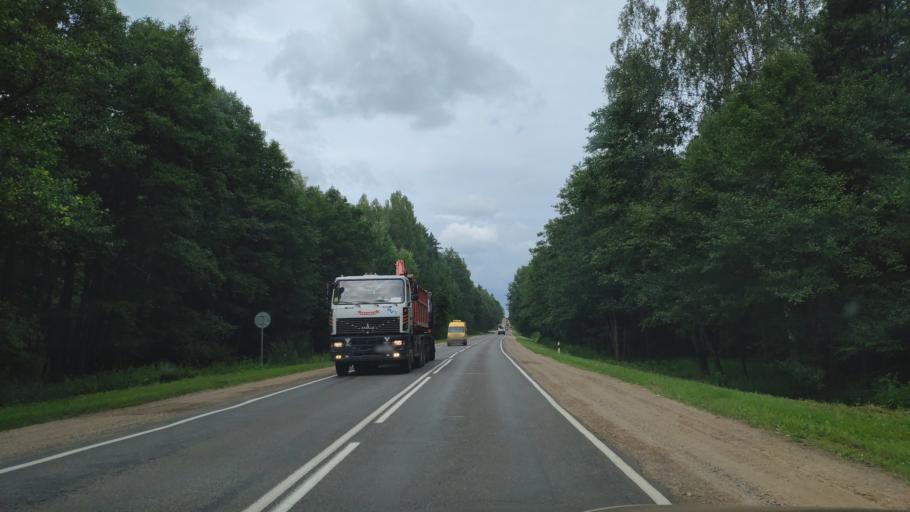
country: BY
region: Minsk
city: Novosel'ye
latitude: 53.9317
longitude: 27.2434
